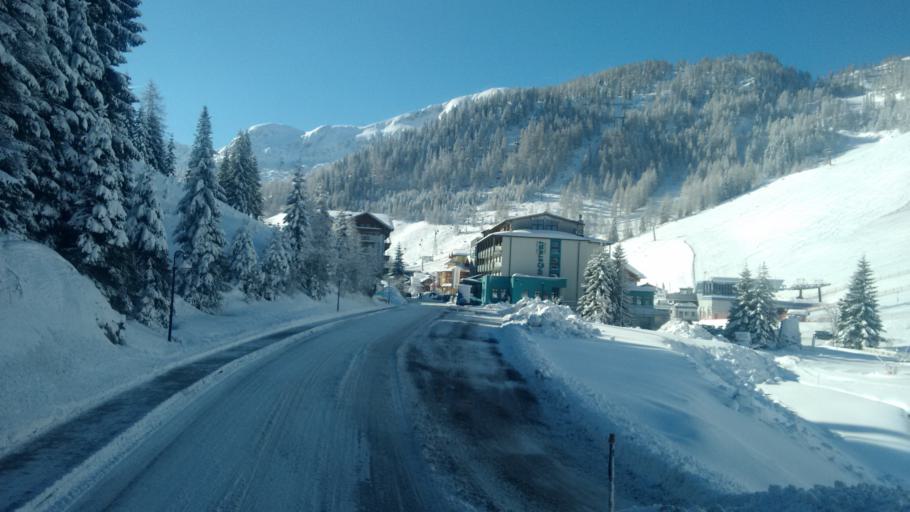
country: AT
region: Salzburg
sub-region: Politischer Bezirk Sankt Johann im Pongau
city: Untertauern
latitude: 47.2960
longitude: 13.4571
